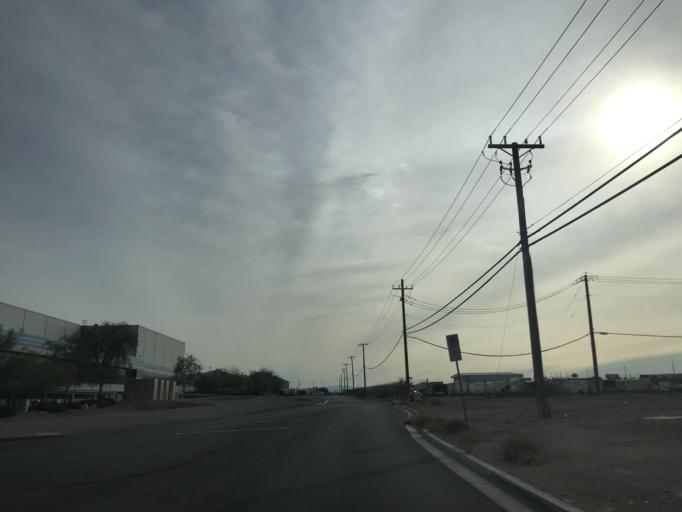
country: US
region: Nevada
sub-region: Clark County
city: Paradise
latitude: 36.0905
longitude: -115.1681
